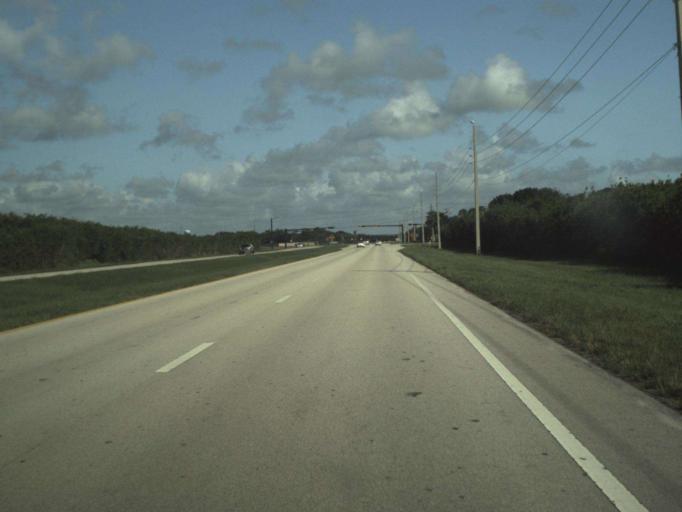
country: US
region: Florida
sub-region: Indian River County
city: Gifford
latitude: 27.6653
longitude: -80.3912
